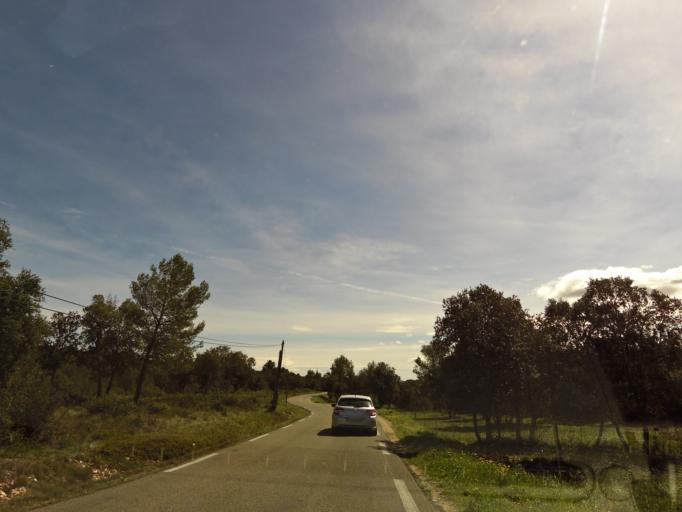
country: FR
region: Languedoc-Roussillon
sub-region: Departement du Gard
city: Langlade
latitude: 43.7880
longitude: 4.2650
